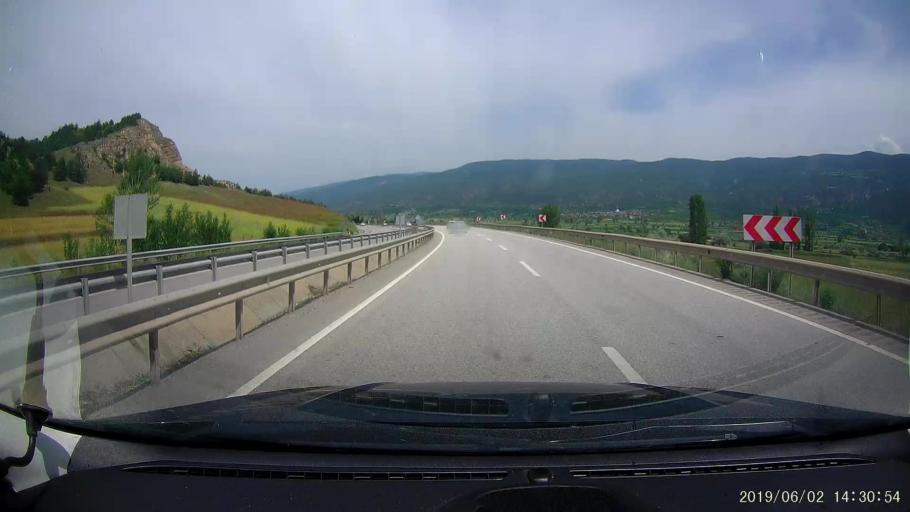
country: TR
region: Kastamonu
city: Tosya
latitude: 41.0151
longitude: 34.1260
